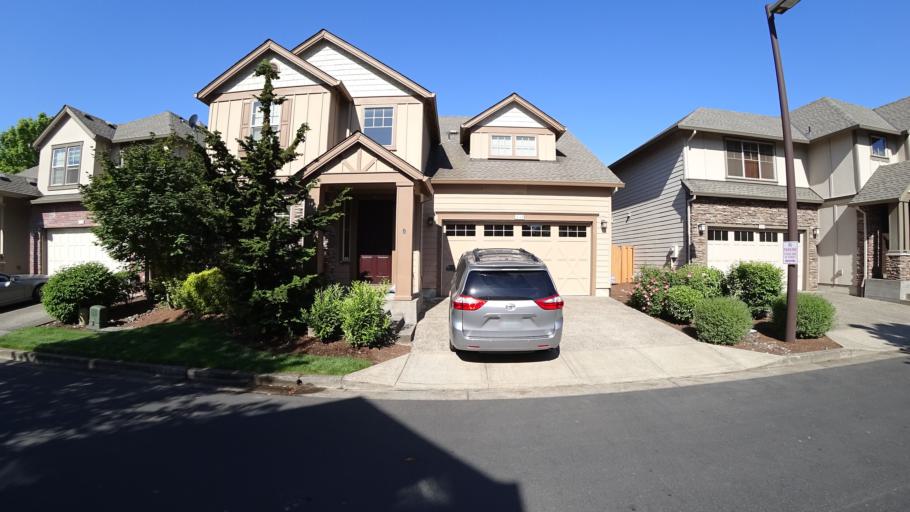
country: US
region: Oregon
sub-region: Washington County
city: Rockcreek
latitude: 45.5228
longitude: -122.9172
